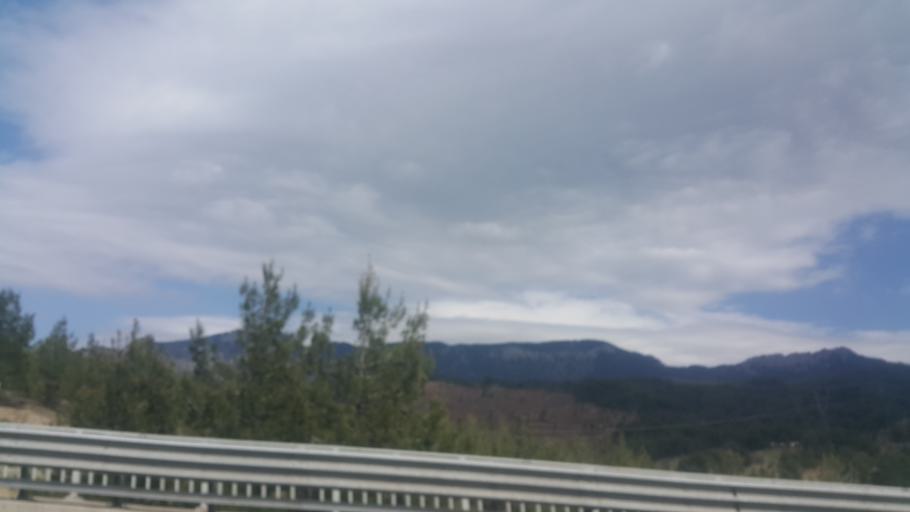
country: TR
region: Adana
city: Pozanti
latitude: 37.4447
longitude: 34.8829
